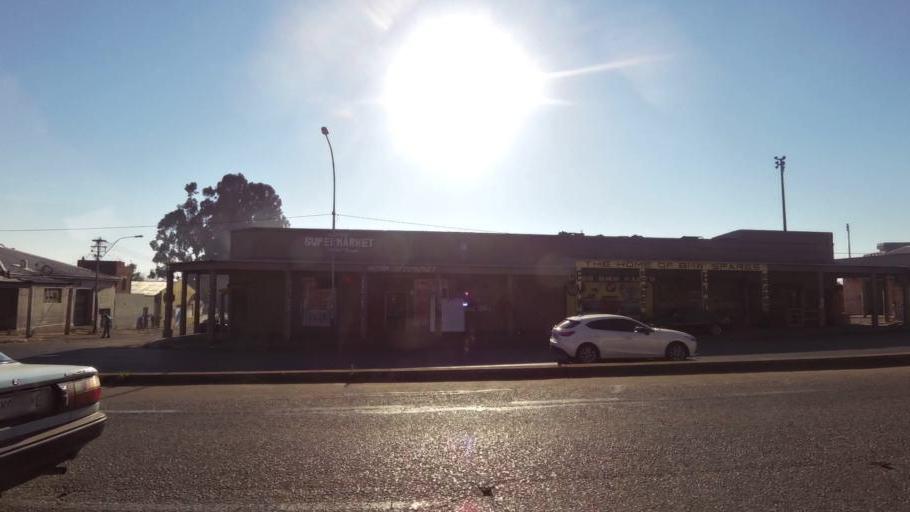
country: ZA
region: Gauteng
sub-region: City of Johannesburg Metropolitan Municipality
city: Johannesburg
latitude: -26.1852
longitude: 27.9823
